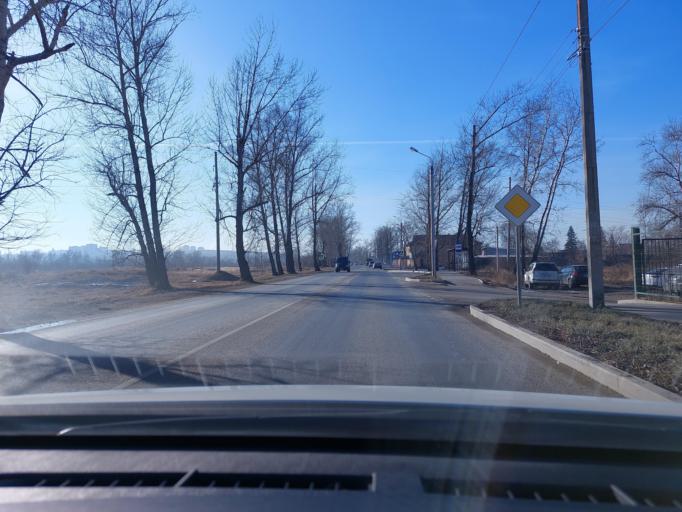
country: RU
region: Irkutsk
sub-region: Irkutskiy Rayon
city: Irkutsk
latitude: 52.3072
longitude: 104.2568
